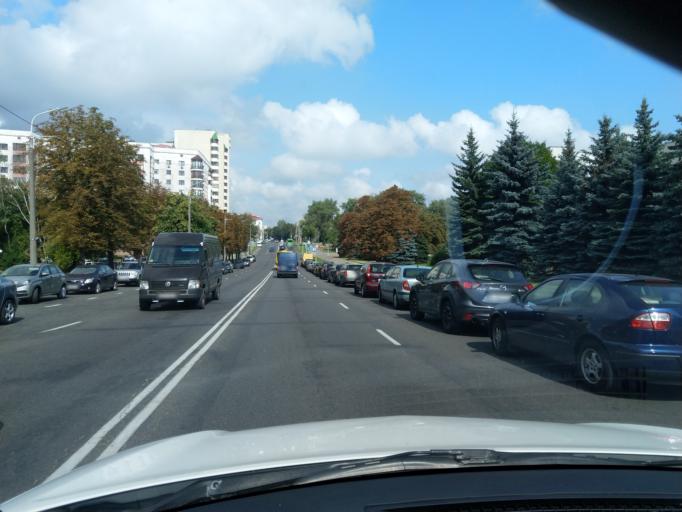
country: BY
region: Minsk
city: Minsk
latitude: 53.9007
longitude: 27.5846
